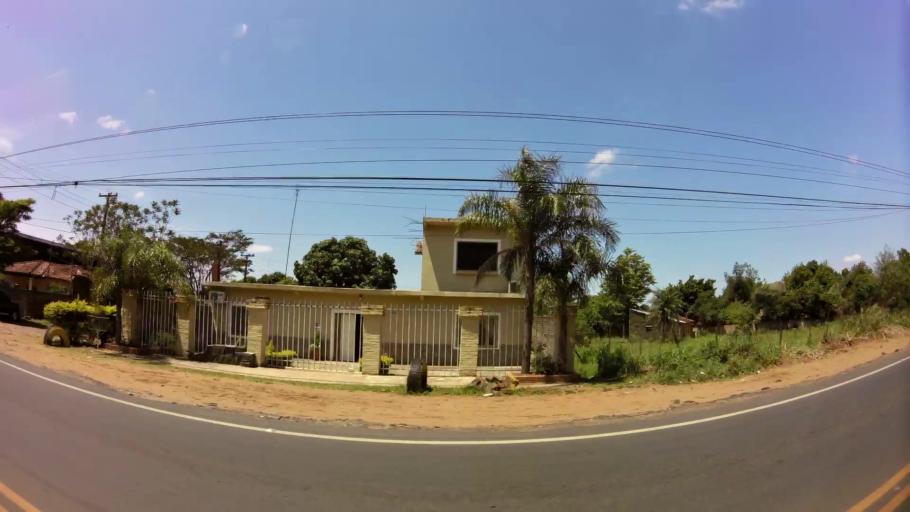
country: PY
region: Central
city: San Antonio
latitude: -25.4097
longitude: -57.5470
